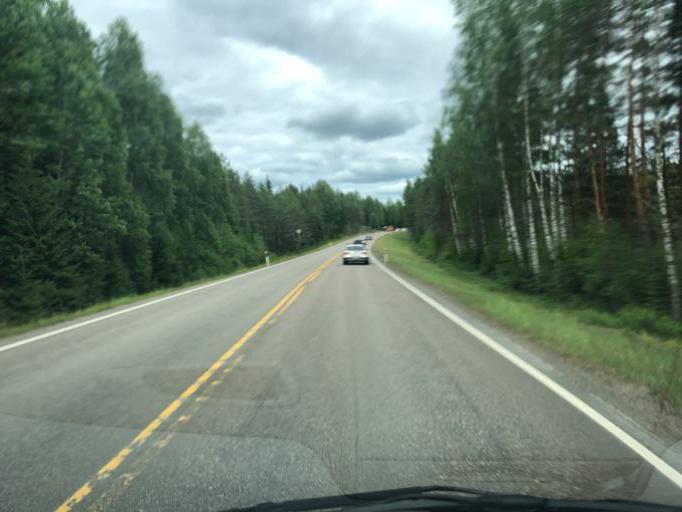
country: FI
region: Kymenlaakso
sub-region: Kouvola
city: Kouvola
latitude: 61.0404
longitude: 26.9947
